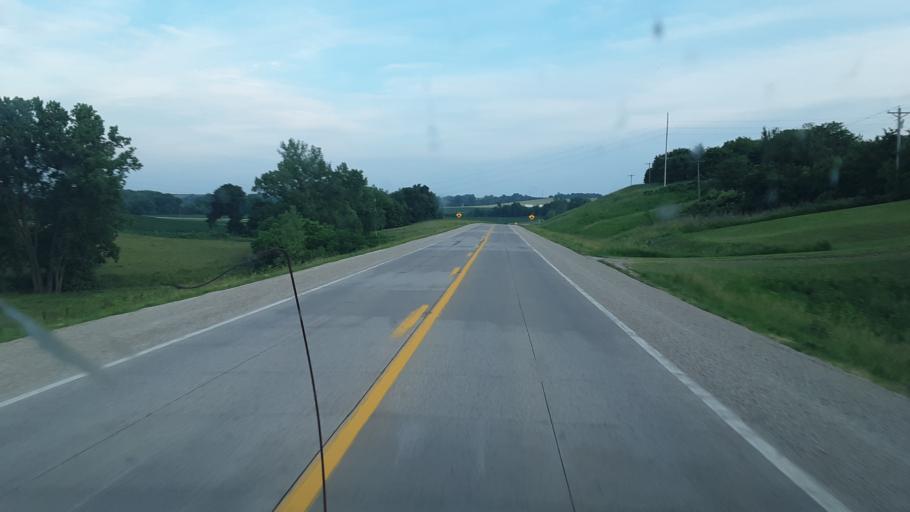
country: US
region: Iowa
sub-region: Benton County
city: Belle Plaine
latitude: 41.7482
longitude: -92.2776
